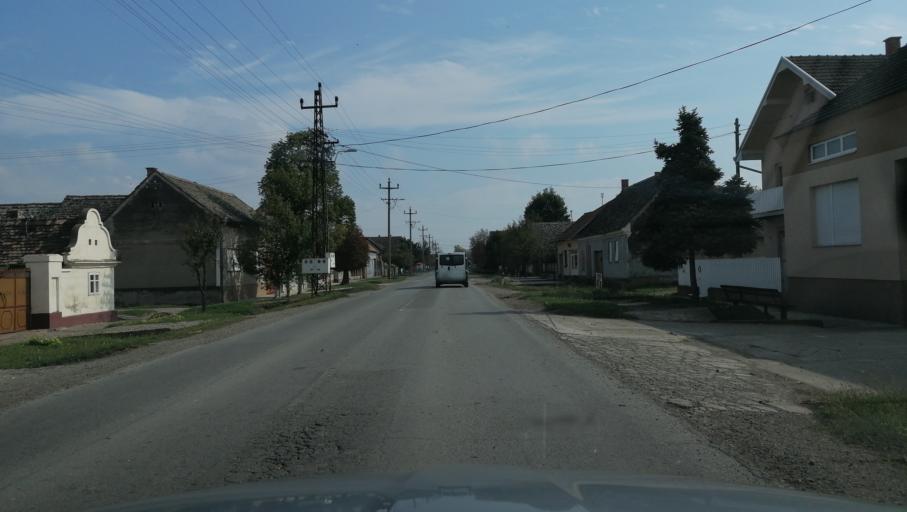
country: RS
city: Ravnje
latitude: 45.0241
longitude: 19.3998
